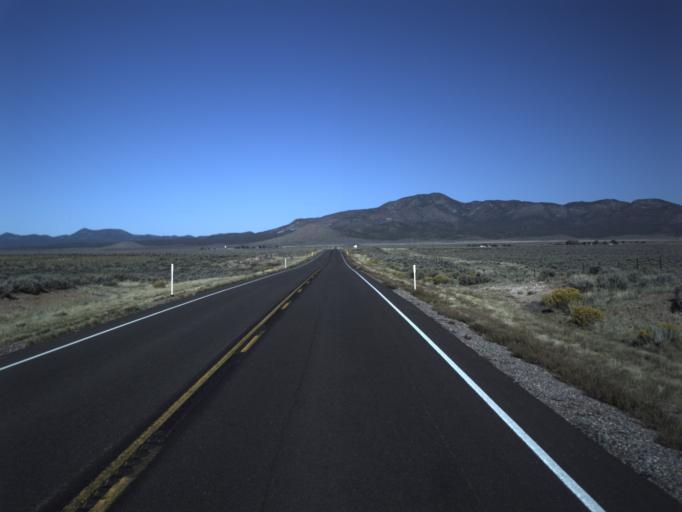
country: US
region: Utah
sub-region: Washington County
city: Enterprise
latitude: 37.7863
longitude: -113.8752
